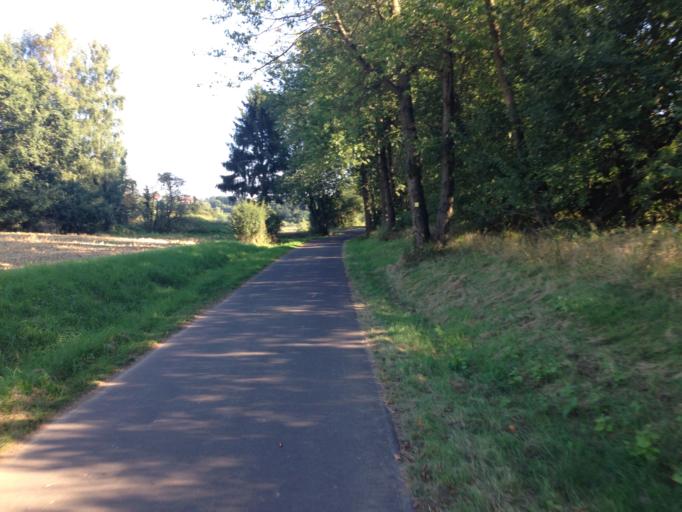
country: DE
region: Hesse
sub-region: Regierungsbezirk Giessen
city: Grunberg
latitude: 50.6027
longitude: 8.9648
